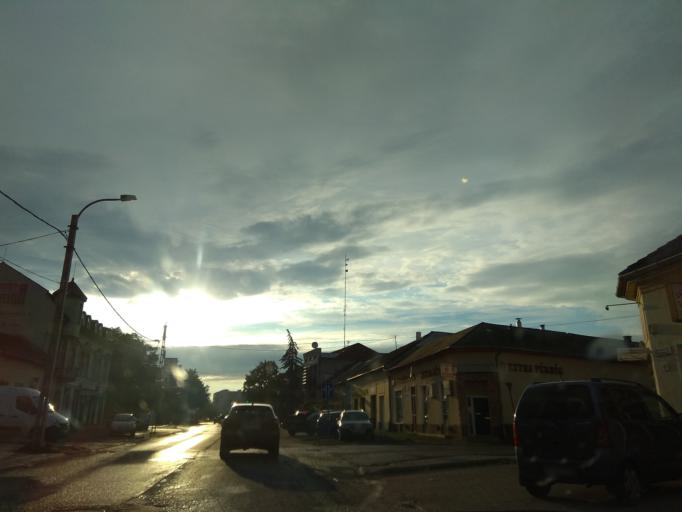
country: HU
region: Borsod-Abauj-Zemplen
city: Miskolc
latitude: 48.0989
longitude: 20.7996
